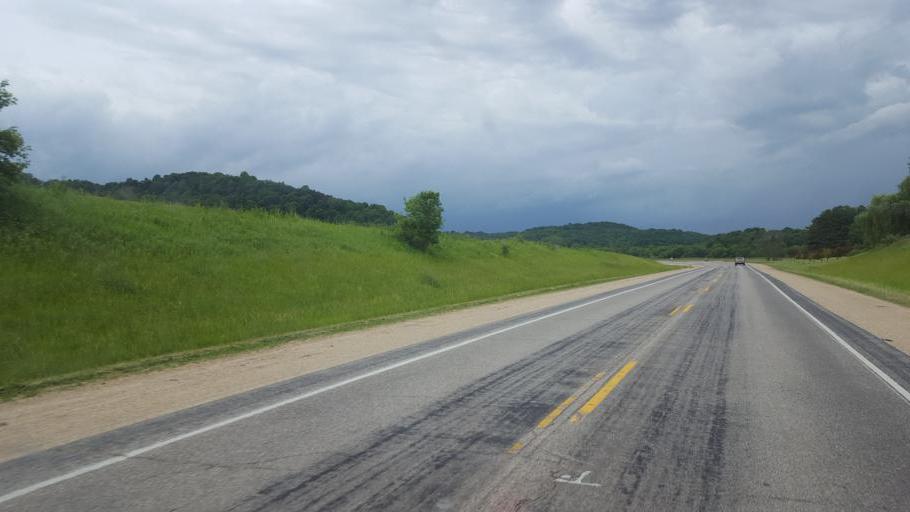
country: US
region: Wisconsin
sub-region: Vernon County
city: Hillsboro
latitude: 43.6599
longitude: -90.3814
